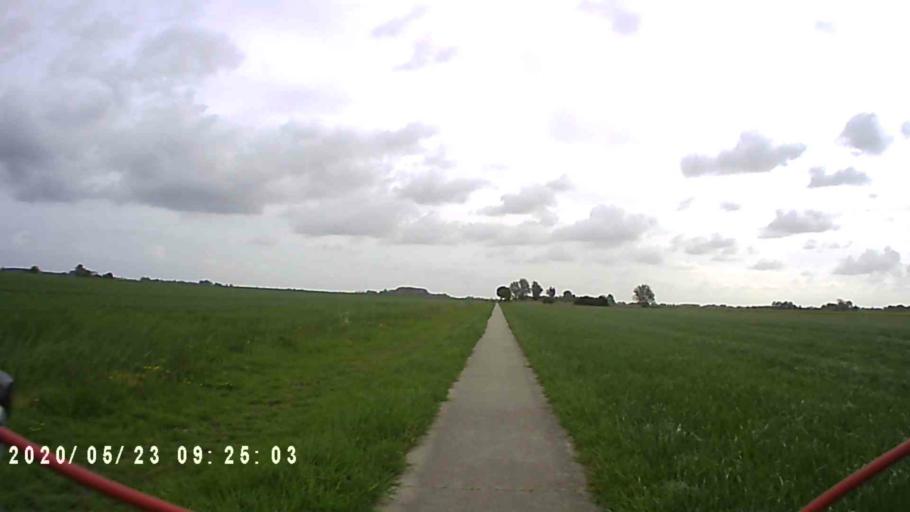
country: NL
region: Groningen
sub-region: Gemeente Bedum
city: Bedum
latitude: 53.2926
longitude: 6.6891
